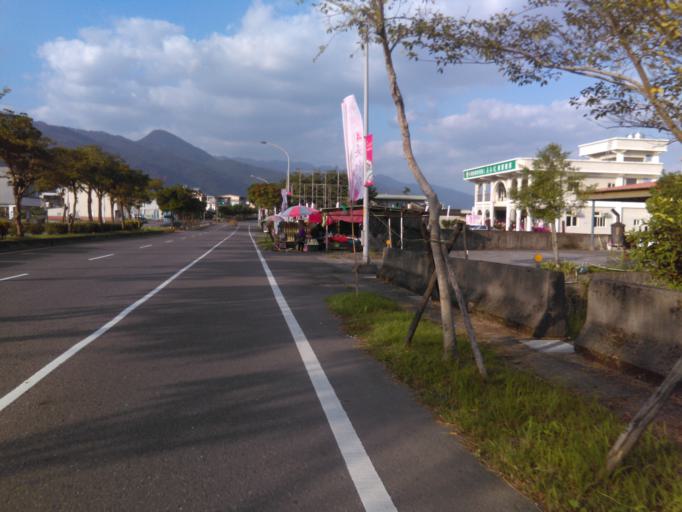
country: TW
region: Taiwan
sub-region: Yilan
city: Yilan
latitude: 24.8038
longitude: 121.7654
